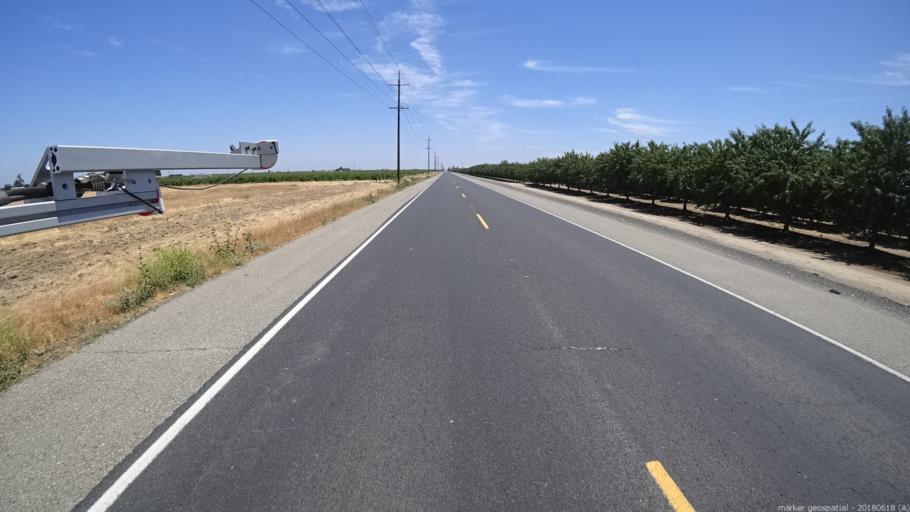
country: US
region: California
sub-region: Madera County
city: Parkwood
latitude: 36.9238
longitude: -120.0886
